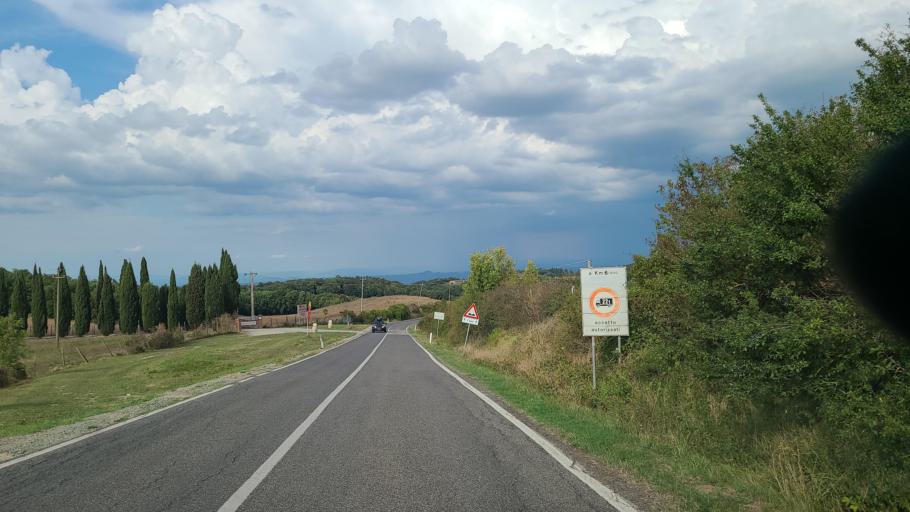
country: IT
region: Tuscany
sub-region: Province of Florence
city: Gambassi Terme
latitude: 43.4829
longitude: 10.9619
